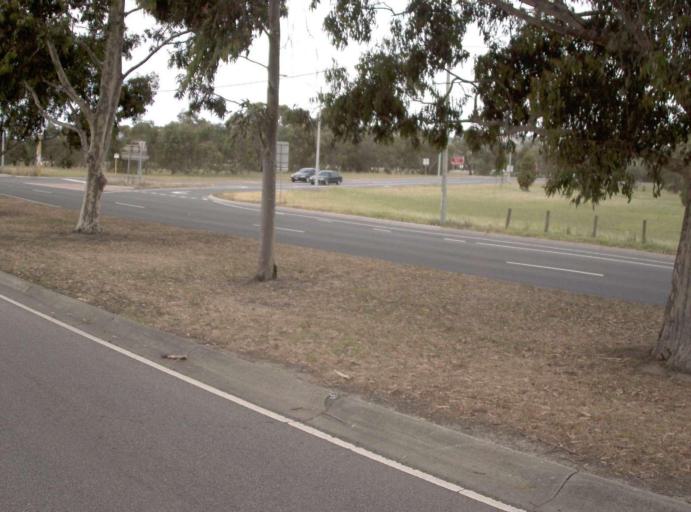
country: AU
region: Victoria
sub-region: Greater Dandenong
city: Dandenong North
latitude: -37.9628
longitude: 145.2248
